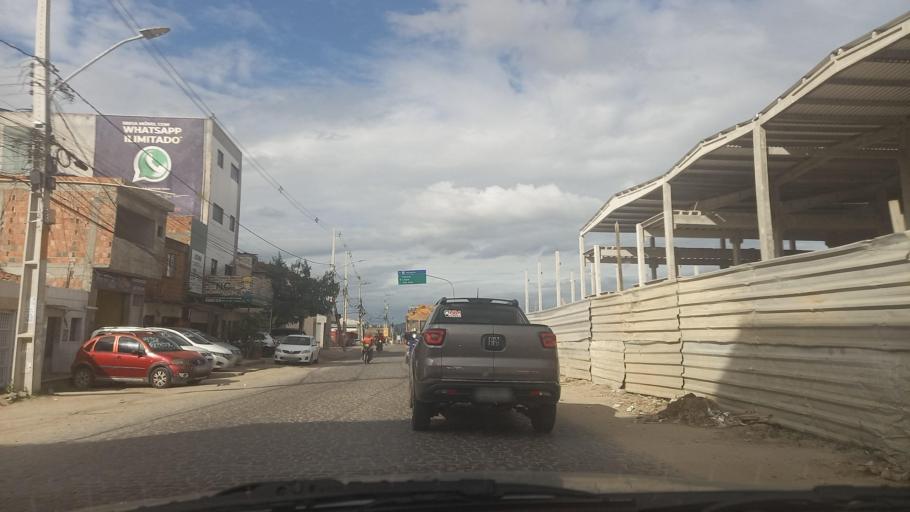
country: BR
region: Pernambuco
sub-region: Caruaru
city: Caruaru
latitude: -8.2875
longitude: -36.0049
